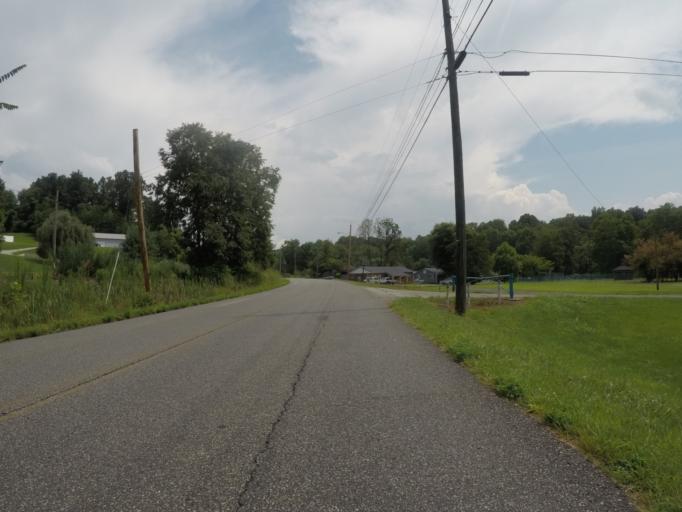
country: US
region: Kentucky
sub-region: Boyd County
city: Ironville
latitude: 38.4621
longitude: -82.6734
